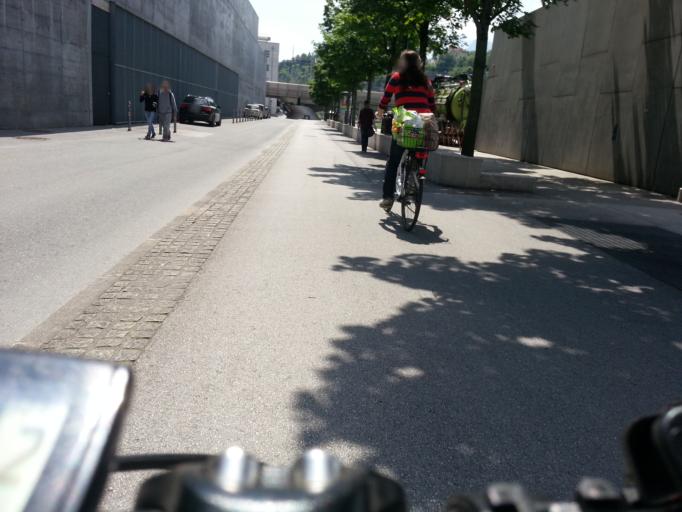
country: AT
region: Salzburg
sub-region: Salzburg Stadt
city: Salzburg
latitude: 47.8099
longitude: 13.0374
